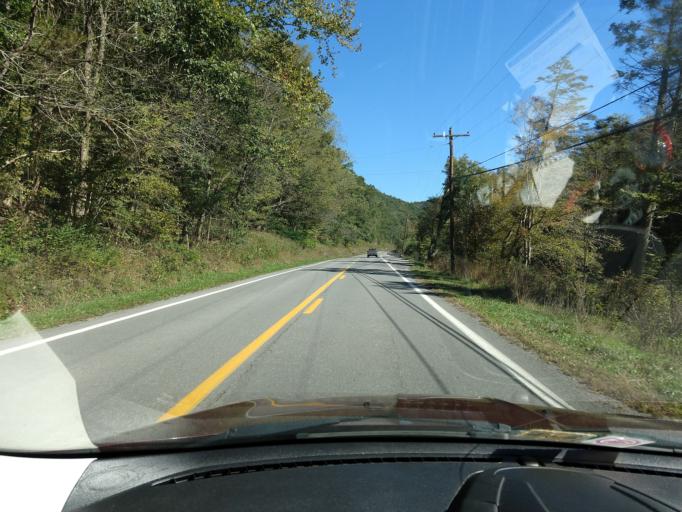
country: US
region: West Virginia
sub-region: Pocahontas County
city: Marlinton
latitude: 38.2133
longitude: -80.0626
